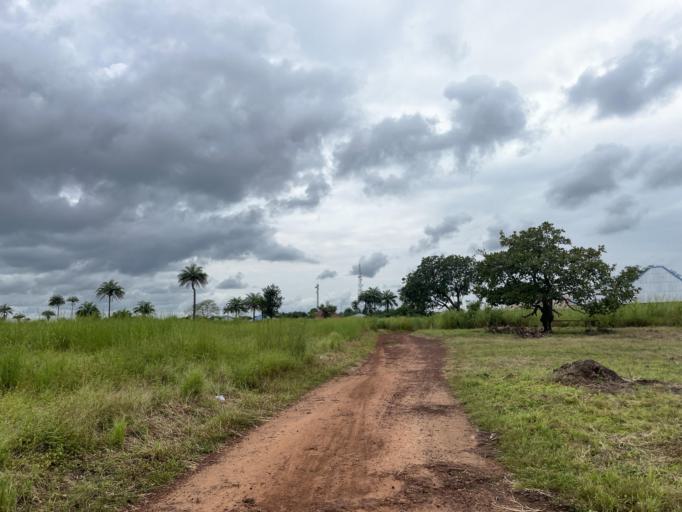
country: SL
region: Northern Province
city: Kambia
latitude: 9.1266
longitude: -12.9009
